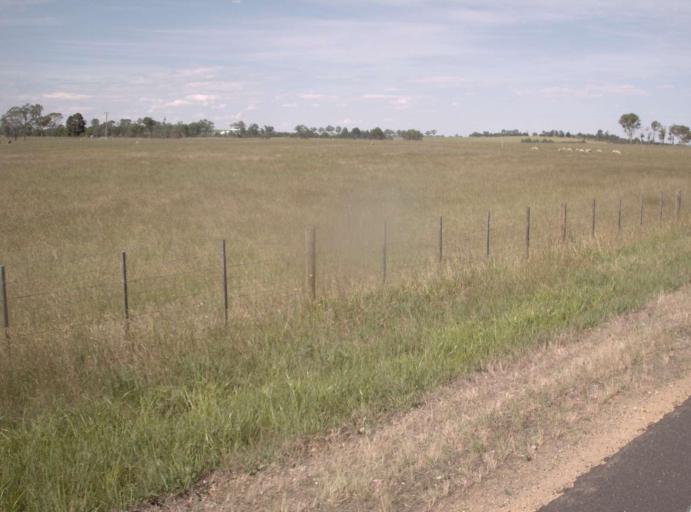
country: AU
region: Victoria
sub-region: East Gippsland
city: Bairnsdale
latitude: -37.8203
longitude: 147.7750
